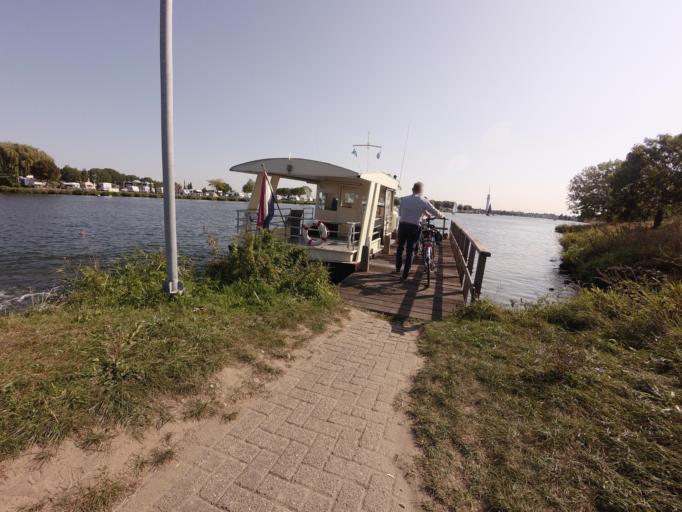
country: NL
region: Limburg
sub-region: Gemeente Roermond
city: Roermond
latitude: 51.1899
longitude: 5.9500
